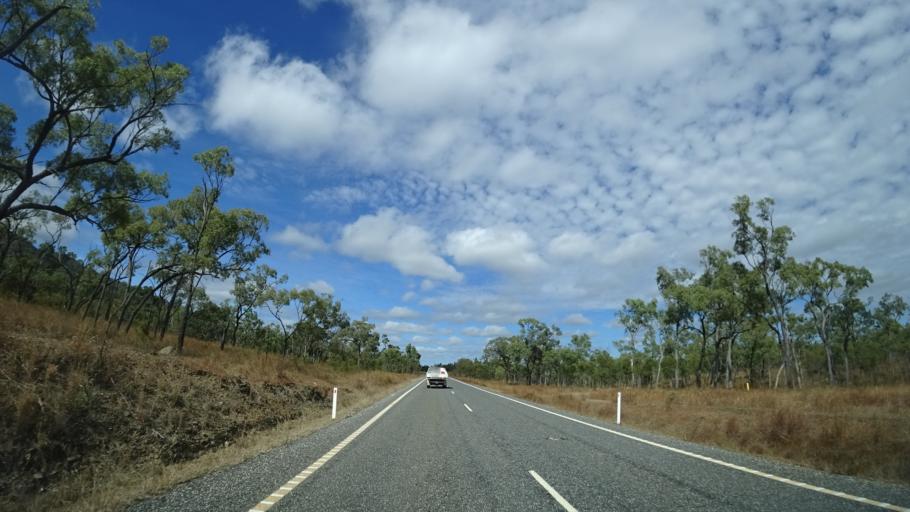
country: AU
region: Queensland
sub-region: Cairns
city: Port Douglas
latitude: -16.3486
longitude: 144.7263
